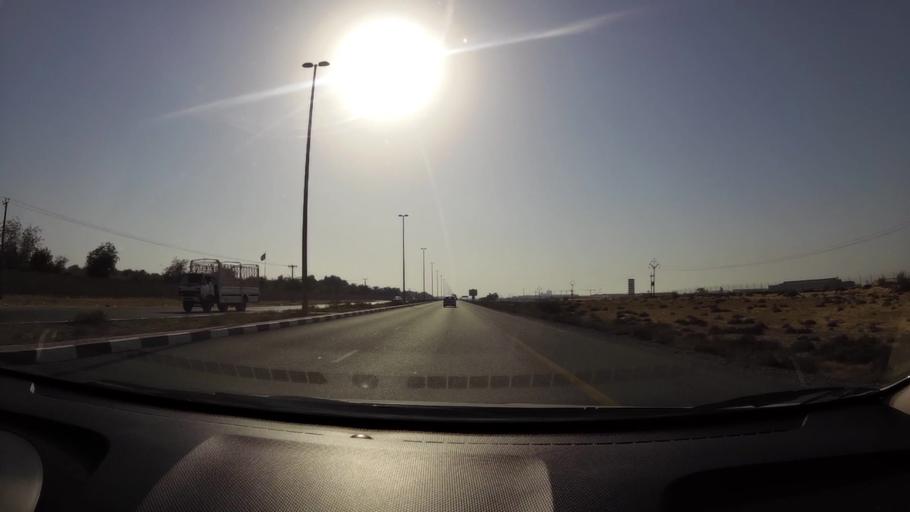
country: AE
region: Umm al Qaywayn
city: Umm al Qaywayn
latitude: 25.4306
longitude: 55.5805
